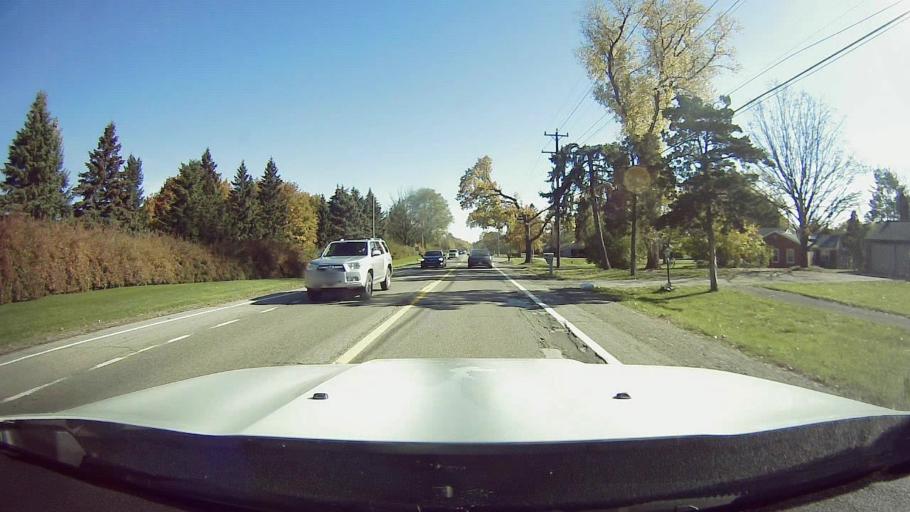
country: US
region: Michigan
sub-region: Oakland County
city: Franklin
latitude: 42.5439
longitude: -83.3245
